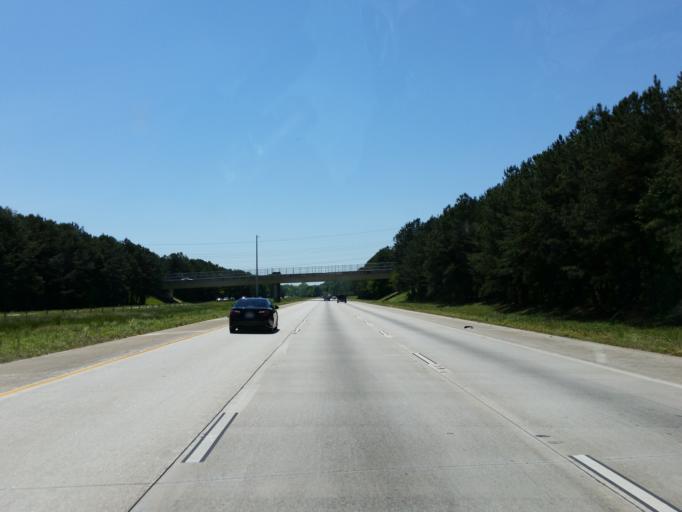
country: US
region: Georgia
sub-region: Clayton County
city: Lake City
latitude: 33.6142
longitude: -84.2969
